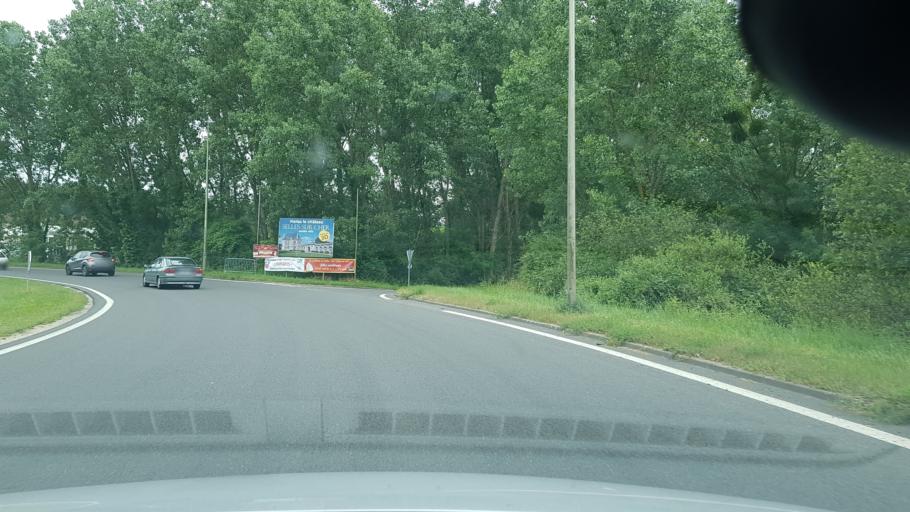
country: FR
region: Centre
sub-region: Departement du Loir-et-Cher
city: Selles-sur-Cher
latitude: 47.2861
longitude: 1.5364
